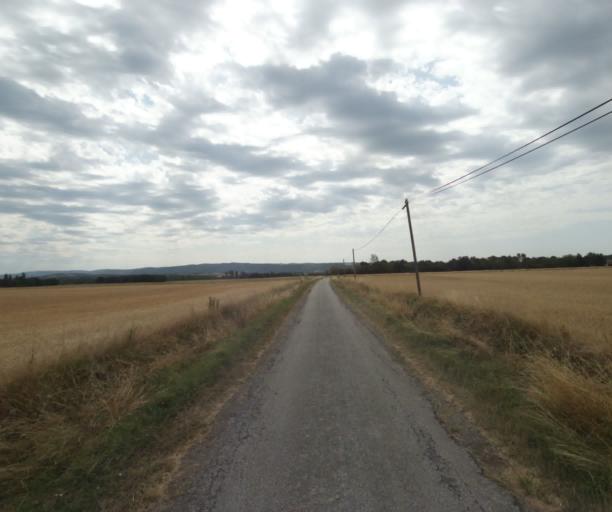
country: FR
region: Midi-Pyrenees
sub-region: Departement de la Haute-Garonne
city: Saint-Felix-Lauragais
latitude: 43.4411
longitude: 1.9283
